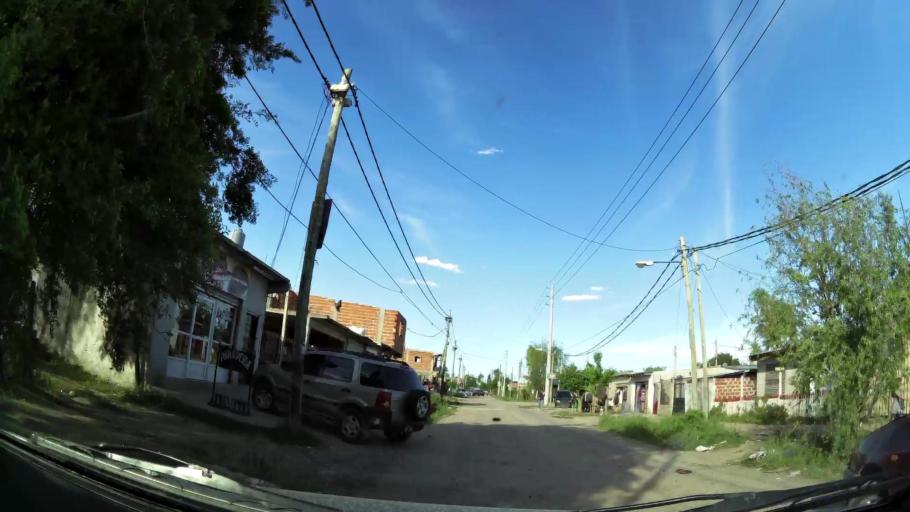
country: AR
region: Buenos Aires
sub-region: Partido de Almirante Brown
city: Adrogue
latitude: -34.8149
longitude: -58.3289
